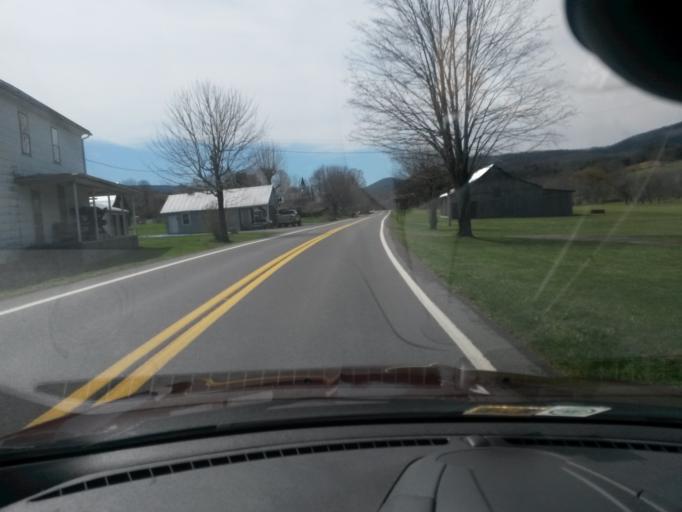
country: US
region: West Virginia
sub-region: Greenbrier County
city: White Sulphur Springs
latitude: 37.6281
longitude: -80.2431
